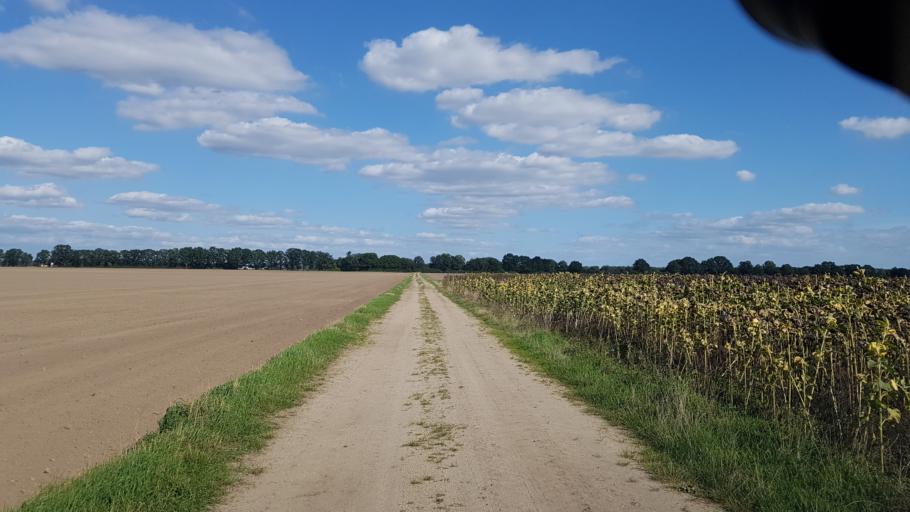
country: DE
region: Brandenburg
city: Sonnewalde
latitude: 51.6809
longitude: 13.6550
